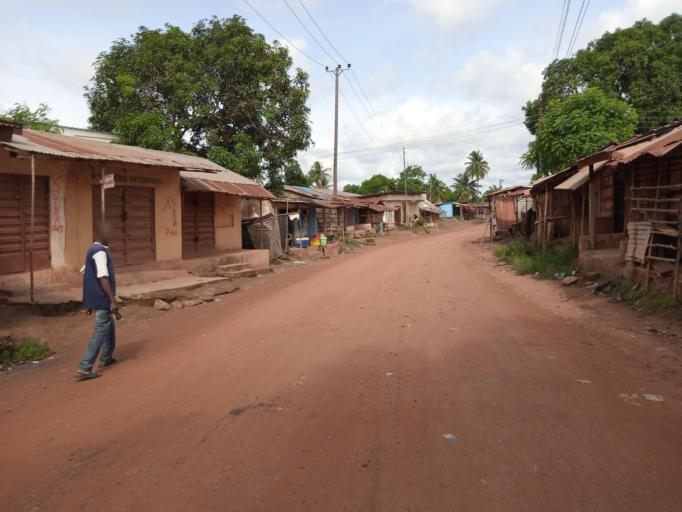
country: SL
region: Southern Province
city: Bo
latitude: 7.9598
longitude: -11.7445
